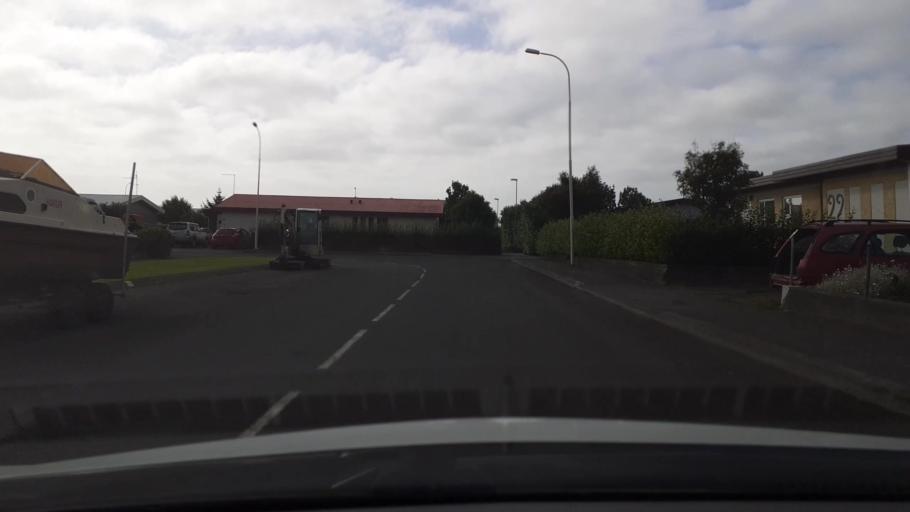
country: IS
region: South
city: THorlakshoefn
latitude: 63.8540
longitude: -21.3926
